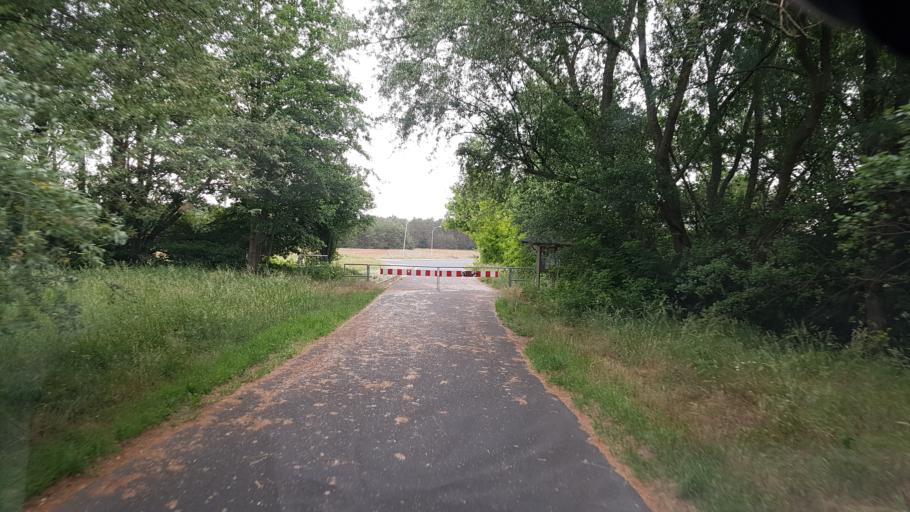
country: DE
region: Saxony-Anhalt
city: Holzdorf
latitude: 51.8195
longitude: 13.2270
